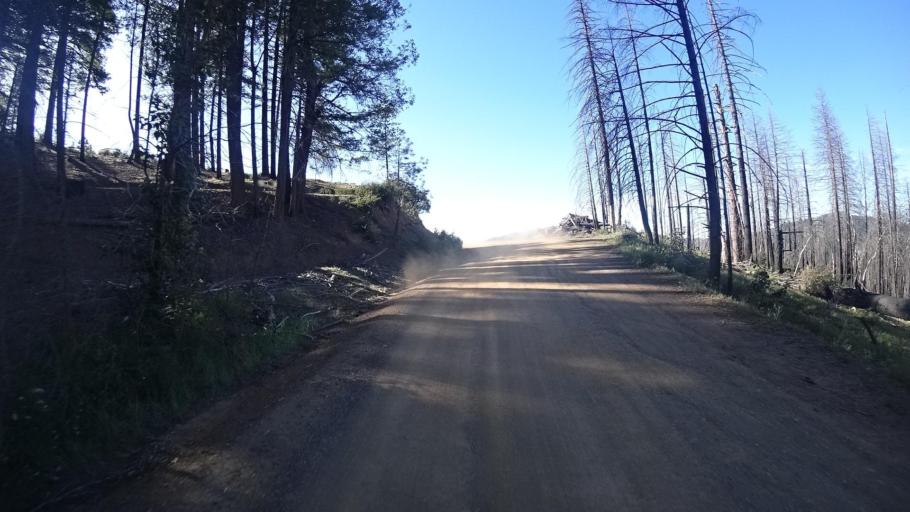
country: US
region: California
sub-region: Lake County
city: Upper Lake
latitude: 39.3590
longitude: -122.9900
